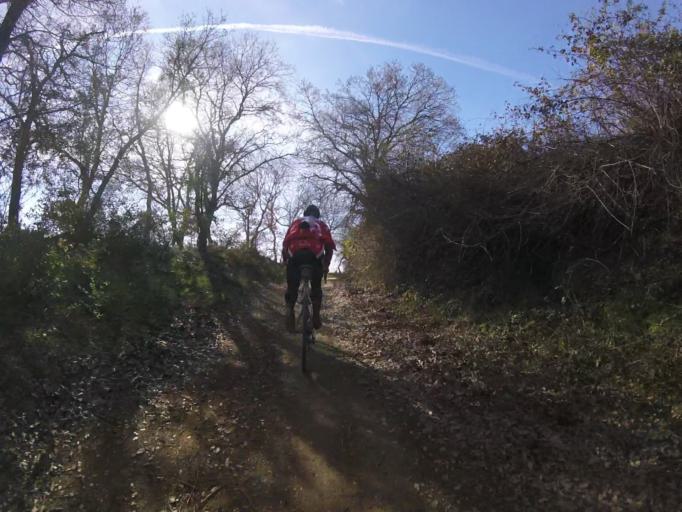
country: ES
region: Navarre
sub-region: Provincia de Navarra
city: Villatuerta
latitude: 42.6709
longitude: -1.9595
